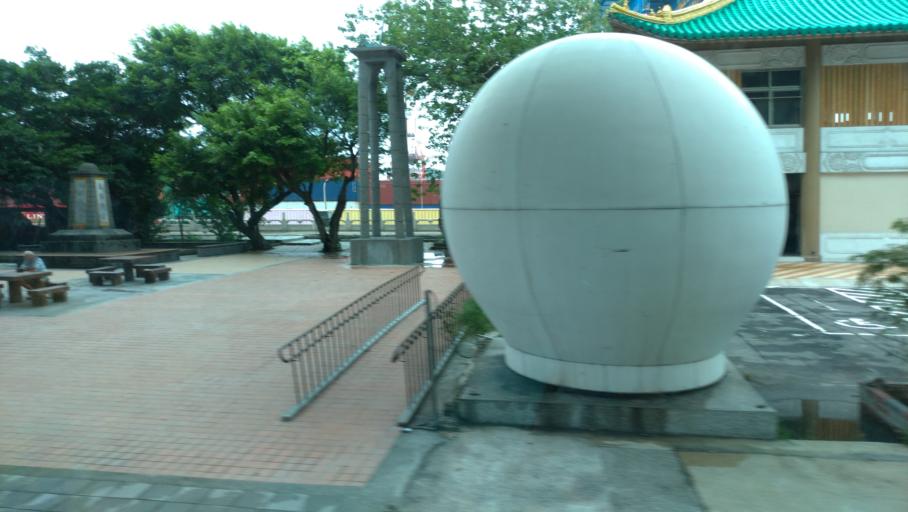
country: TW
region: Taiwan
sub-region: Keelung
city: Keelung
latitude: 25.1409
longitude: 121.7564
